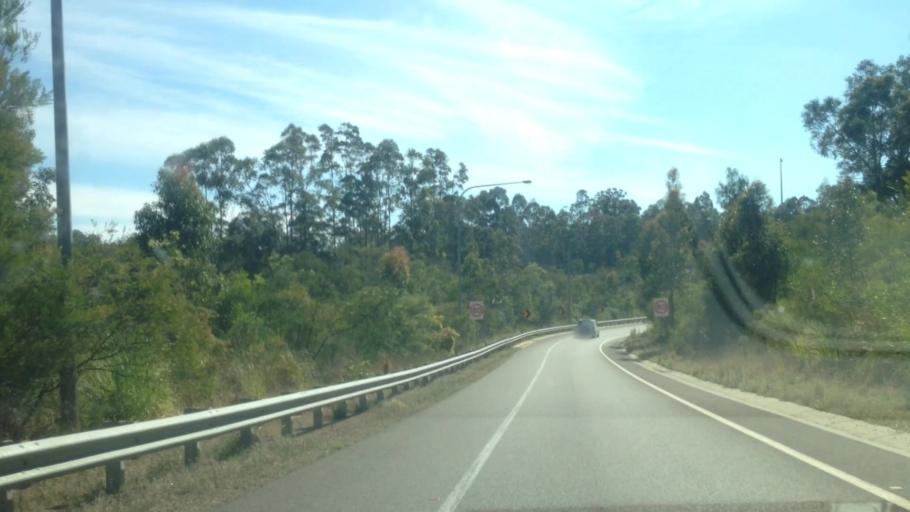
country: AU
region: New South Wales
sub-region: Lake Macquarie Shire
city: Holmesville
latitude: -32.8895
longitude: 151.5976
